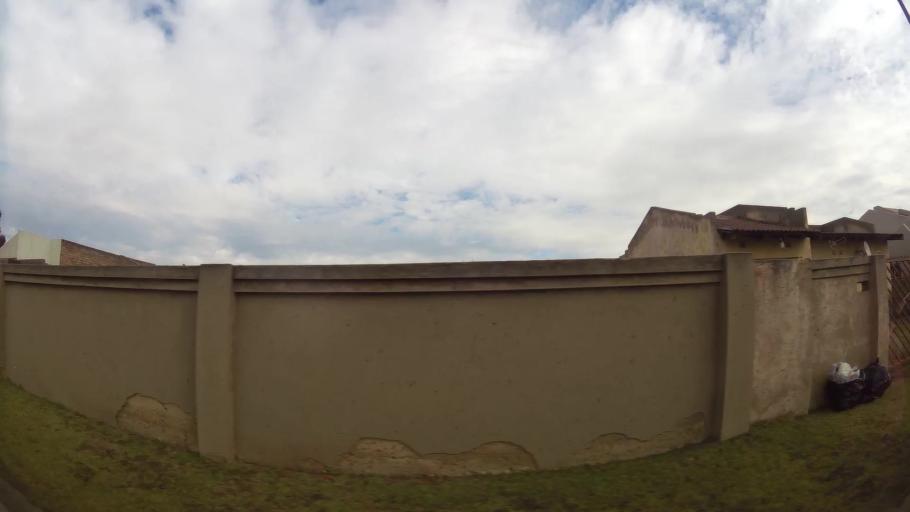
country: ZA
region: Gauteng
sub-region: Ekurhuleni Metropolitan Municipality
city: Germiston
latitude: -26.3241
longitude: 28.1783
